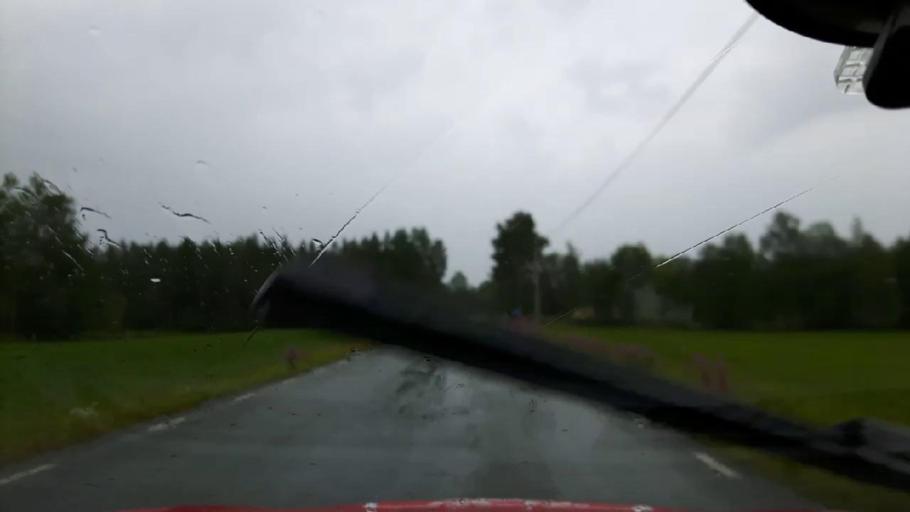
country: SE
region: Jaemtland
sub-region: OEstersunds Kommun
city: Brunflo
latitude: 62.9912
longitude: 14.7959
